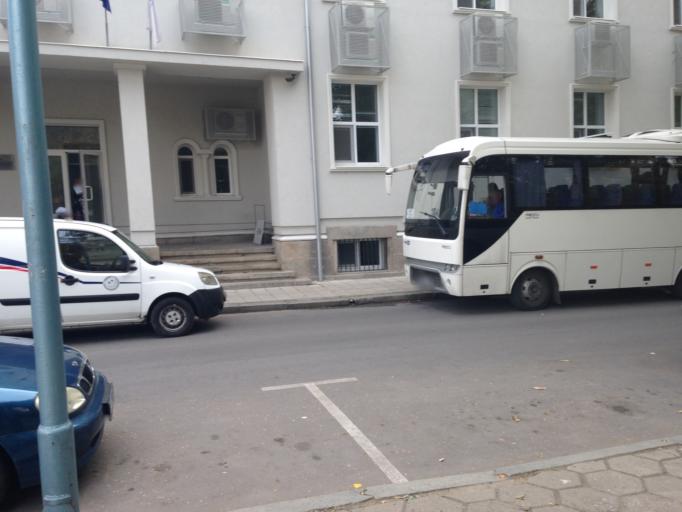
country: BG
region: Plovdiv
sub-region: Obshtina Plovdiv
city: Plovdiv
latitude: 42.1486
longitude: 24.7435
